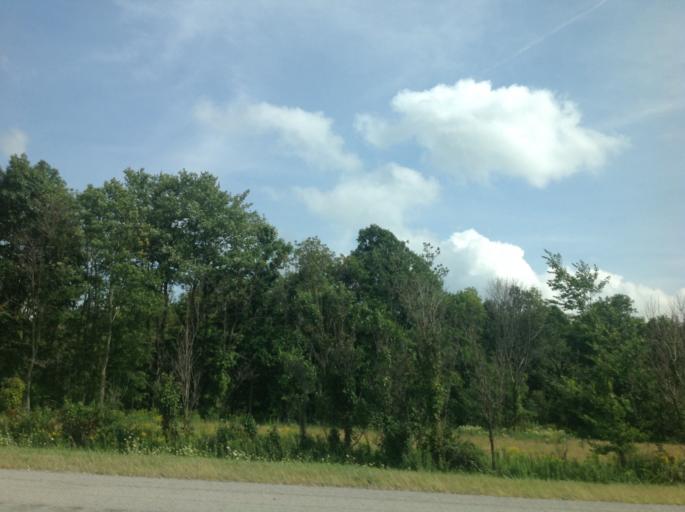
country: US
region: Ohio
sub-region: Sandusky County
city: Bellville
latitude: 40.5799
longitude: -82.6024
